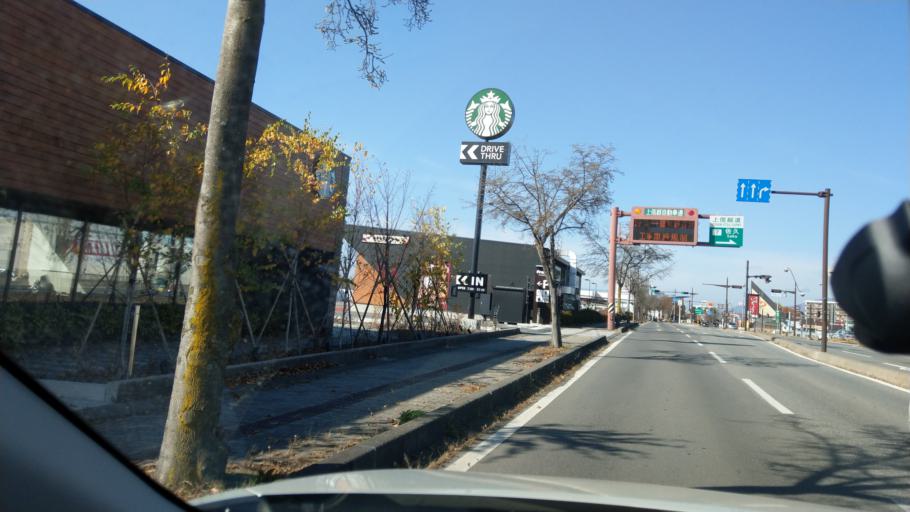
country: JP
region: Nagano
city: Komoro
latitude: 36.2841
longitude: 138.4814
